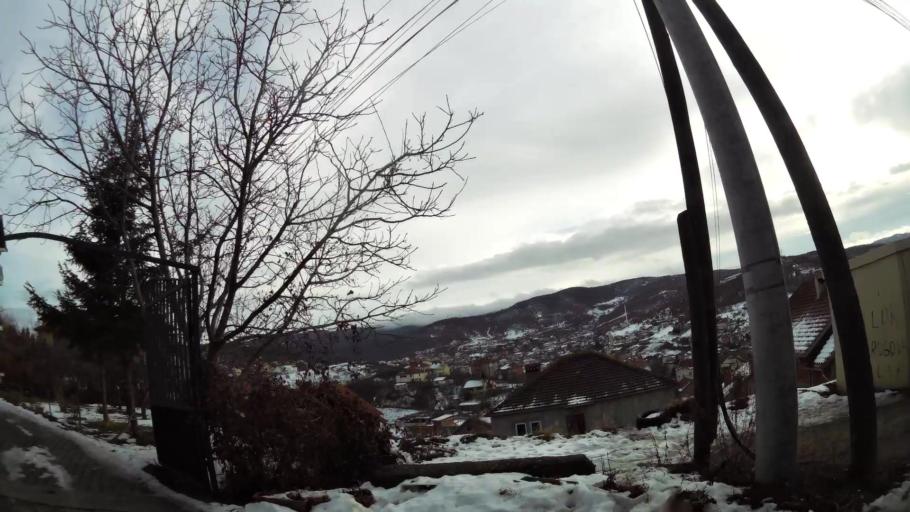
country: XK
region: Pristina
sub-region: Komuna e Prishtines
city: Pristina
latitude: 42.6680
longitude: 21.1821
